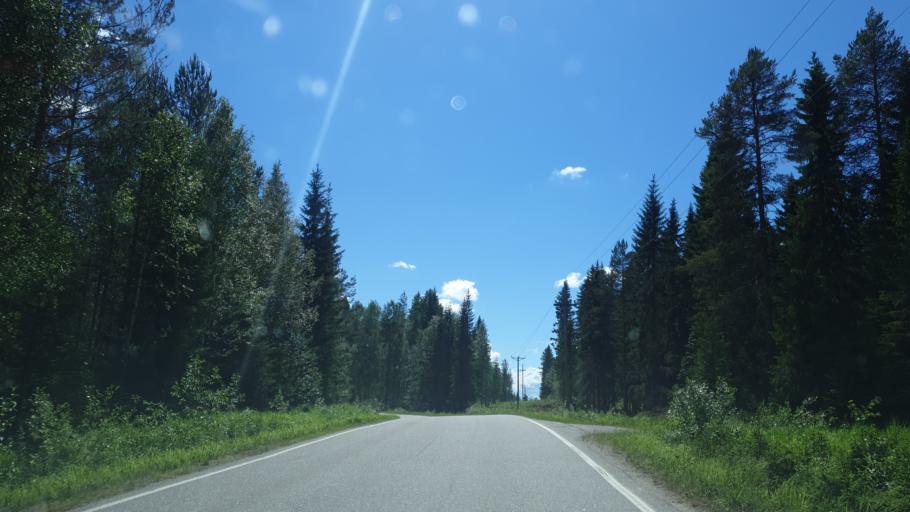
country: FI
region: Northern Savo
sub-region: Koillis-Savo
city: Kaavi
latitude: 63.0342
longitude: 28.5519
